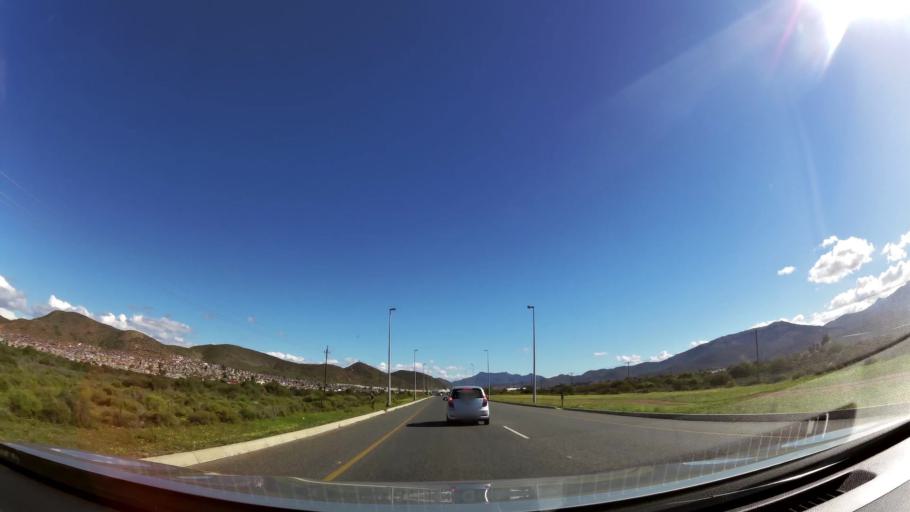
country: ZA
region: Western Cape
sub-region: Cape Winelands District Municipality
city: Ashton
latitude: -33.8148
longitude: 19.9039
